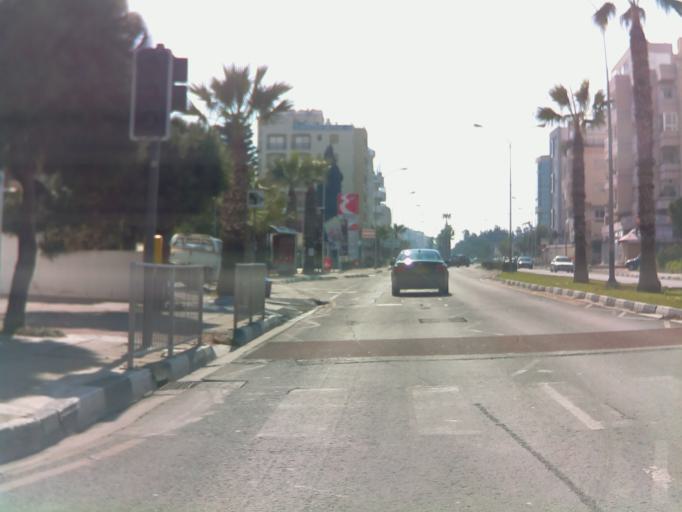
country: CY
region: Larnaka
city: Larnaca
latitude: 34.9101
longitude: 33.6293
